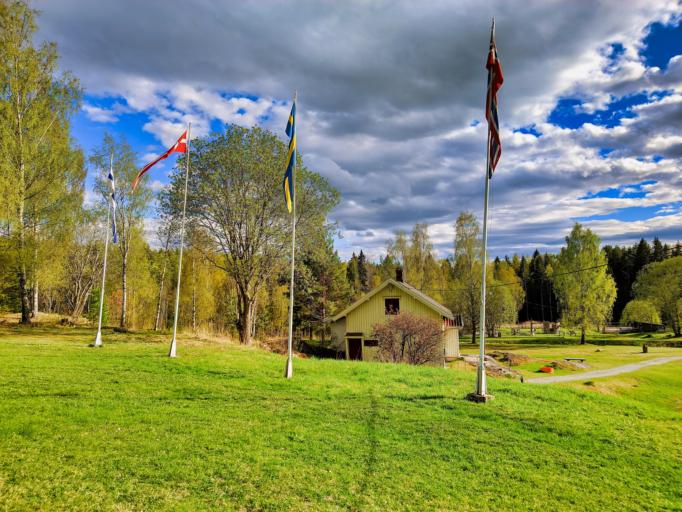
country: NO
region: Hedmark
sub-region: Loten
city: Loten
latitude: 60.7870
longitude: 11.3138
